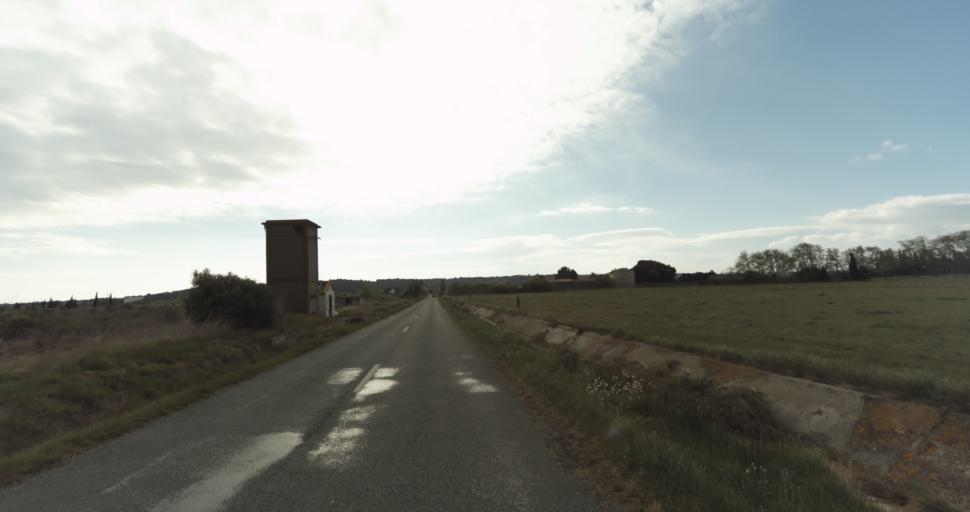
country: FR
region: Languedoc-Roussillon
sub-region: Departement de l'Aude
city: Leucate
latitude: 42.9314
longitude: 2.9982
